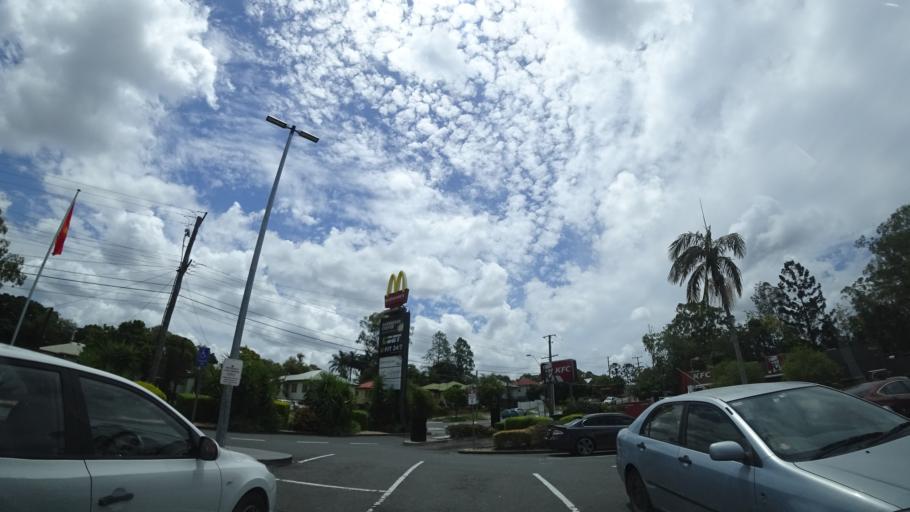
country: AU
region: Queensland
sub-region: Moreton Bay
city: Ferny Hills
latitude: -27.4041
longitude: 152.9621
